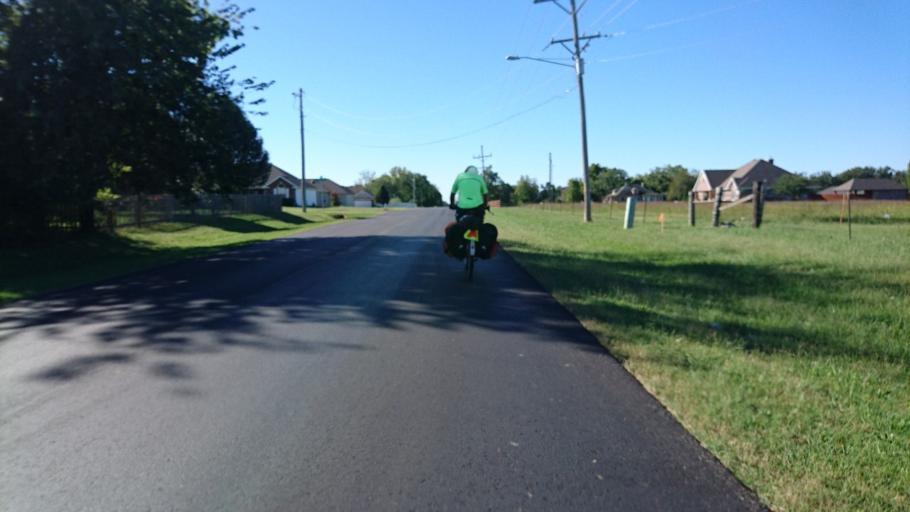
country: US
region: Missouri
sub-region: Jasper County
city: Webb City
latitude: 37.1207
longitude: -94.4937
